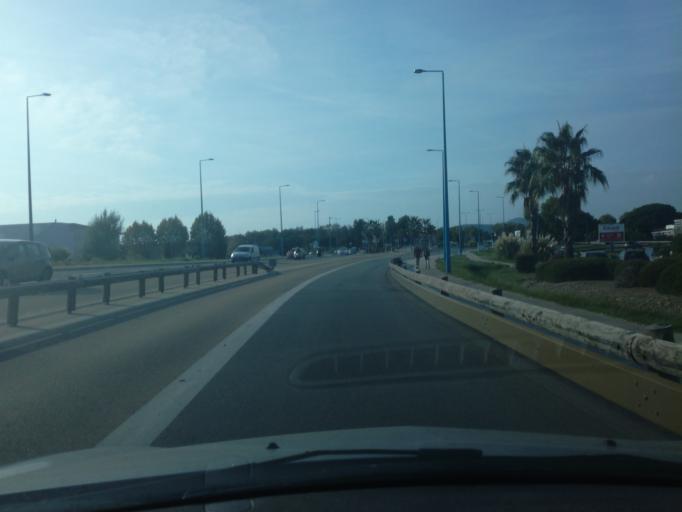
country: FR
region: Provence-Alpes-Cote d'Azur
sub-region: Departement des Alpes-Maritimes
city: Mandelieu-la-Napoule
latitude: 43.5519
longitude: 6.9471
